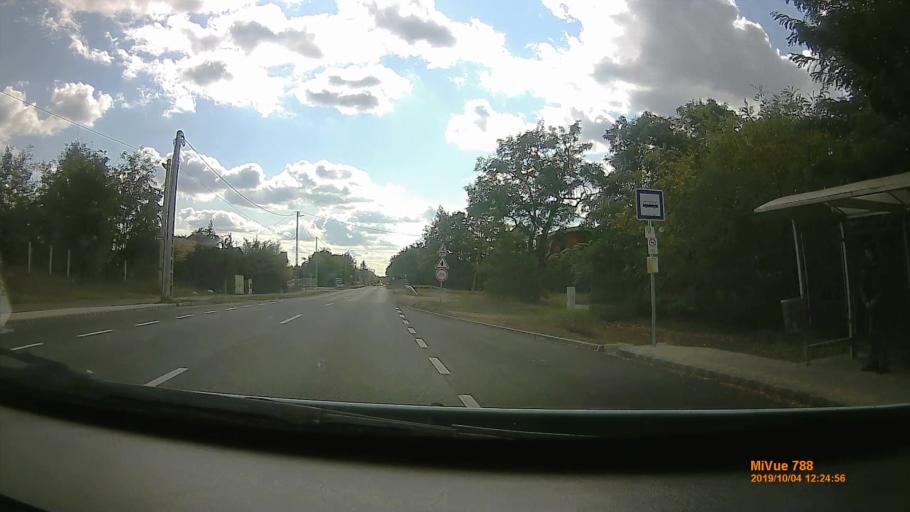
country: HU
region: Szabolcs-Szatmar-Bereg
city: Nyiregyhaza
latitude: 47.9913
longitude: 21.7039
